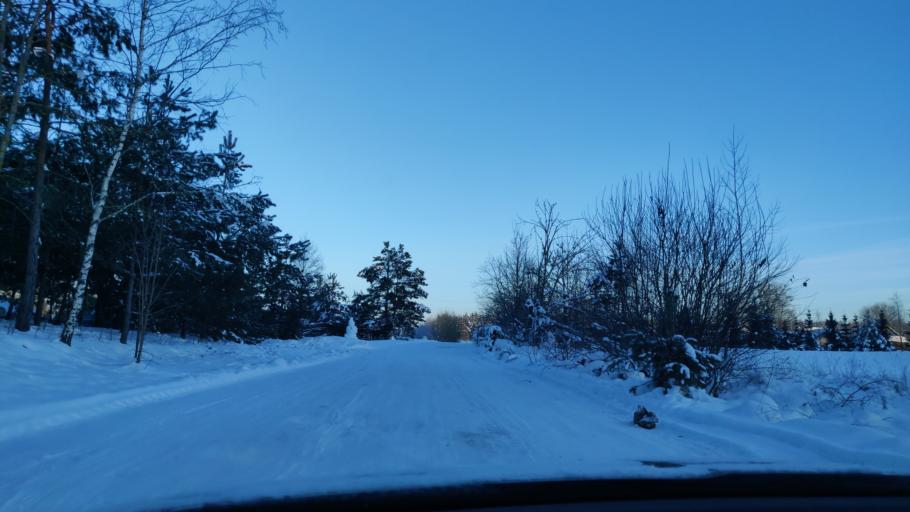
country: LT
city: Trakai
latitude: 54.6133
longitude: 24.9350
